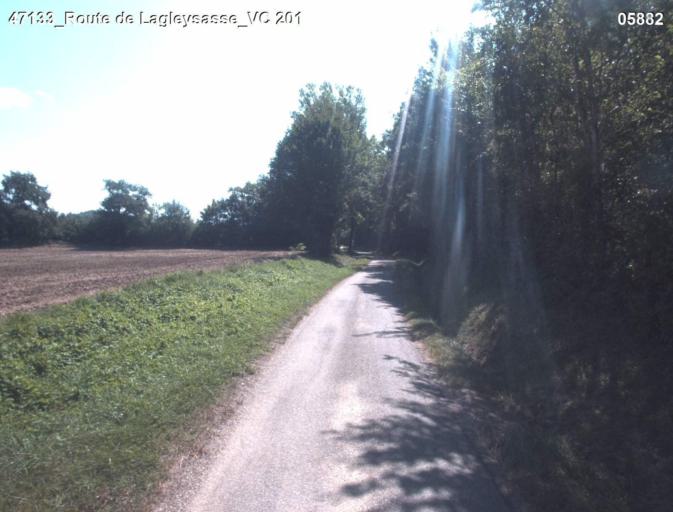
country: FR
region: Aquitaine
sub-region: Departement du Lot-et-Garonne
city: Laplume
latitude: 44.0678
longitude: 0.4943
